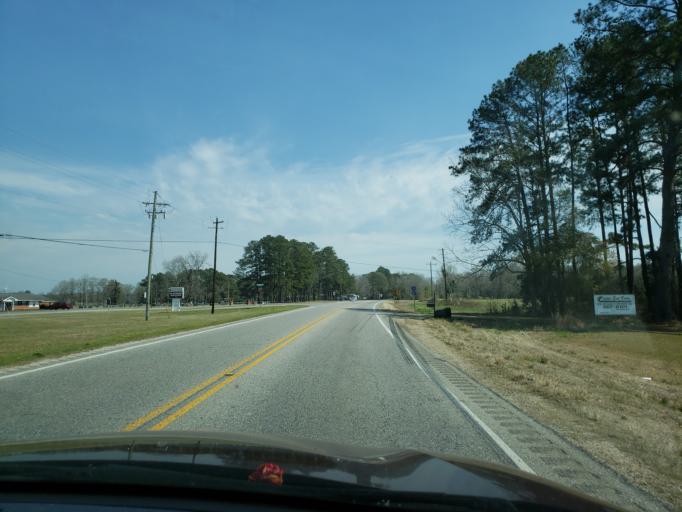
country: US
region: Alabama
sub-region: Elmore County
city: Elmore
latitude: 32.5497
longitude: -86.2885
